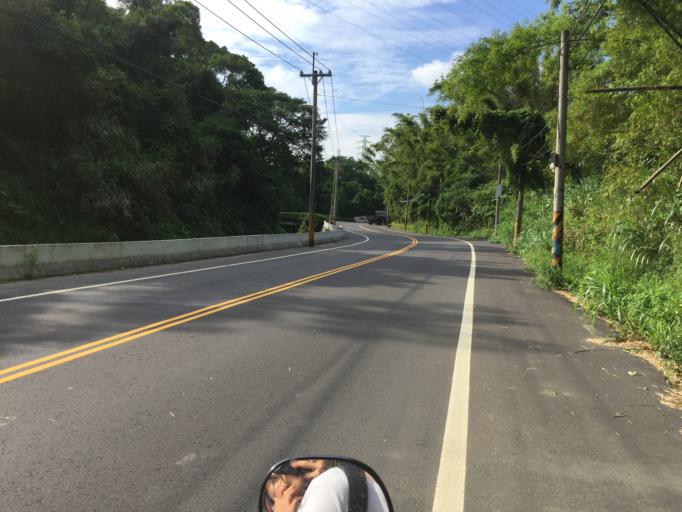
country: TW
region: Taiwan
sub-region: Hsinchu
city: Hsinchu
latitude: 24.7643
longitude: 120.9424
